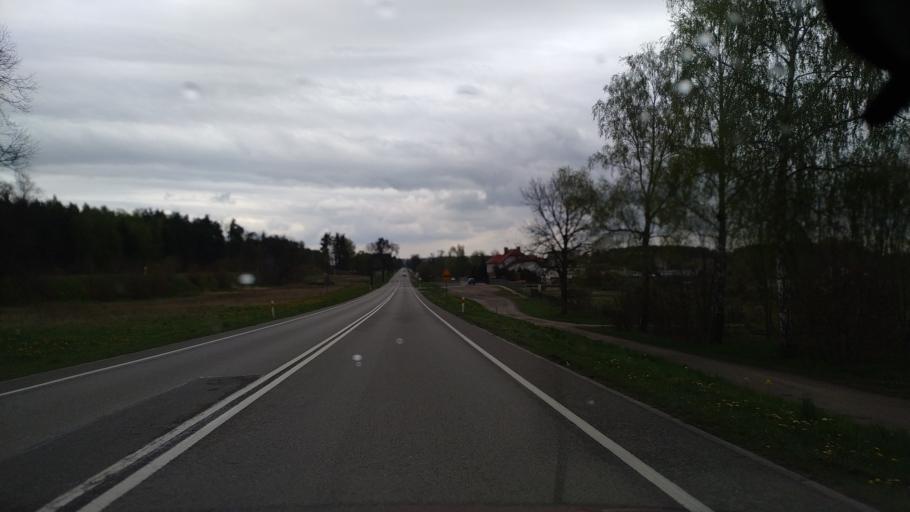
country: PL
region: Pomeranian Voivodeship
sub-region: Powiat tczewski
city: Pelplin
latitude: 54.0229
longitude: 18.6371
